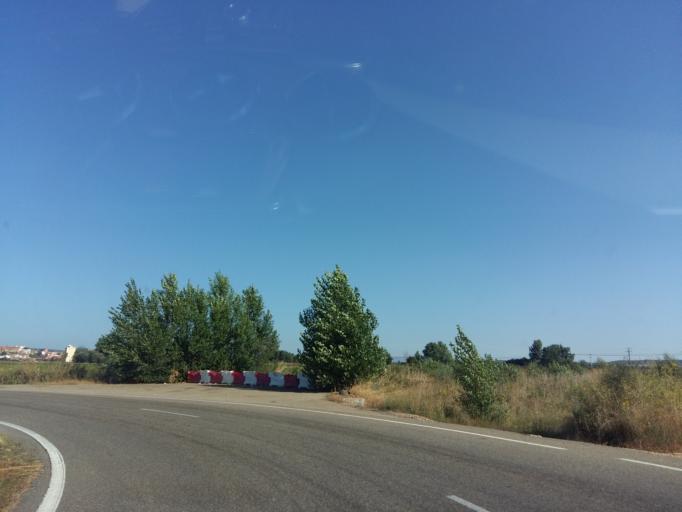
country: ES
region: Castille and Leon
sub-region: Provincia de Leon
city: Astorga
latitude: 42.4408
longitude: -6.0383
